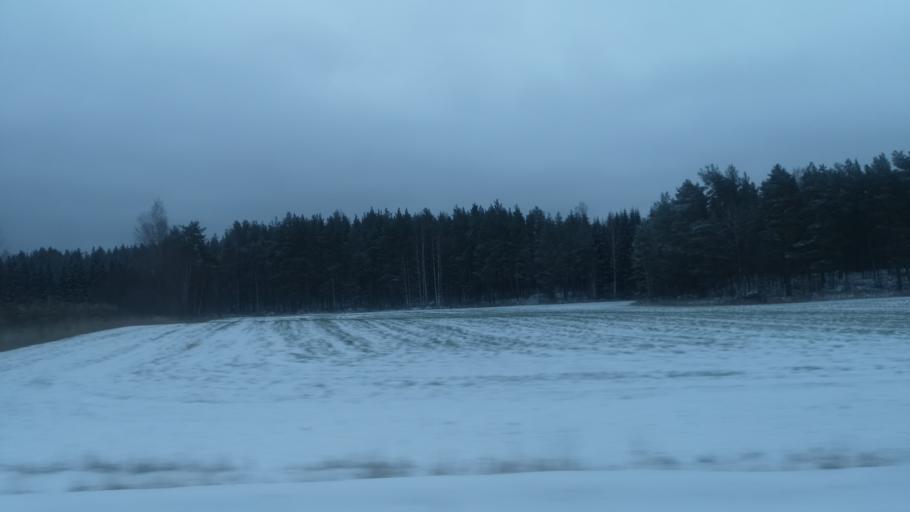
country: FI
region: Southern Savonia
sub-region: Savonlinna
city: Enonkoski
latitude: 62.0900
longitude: 28.6774
